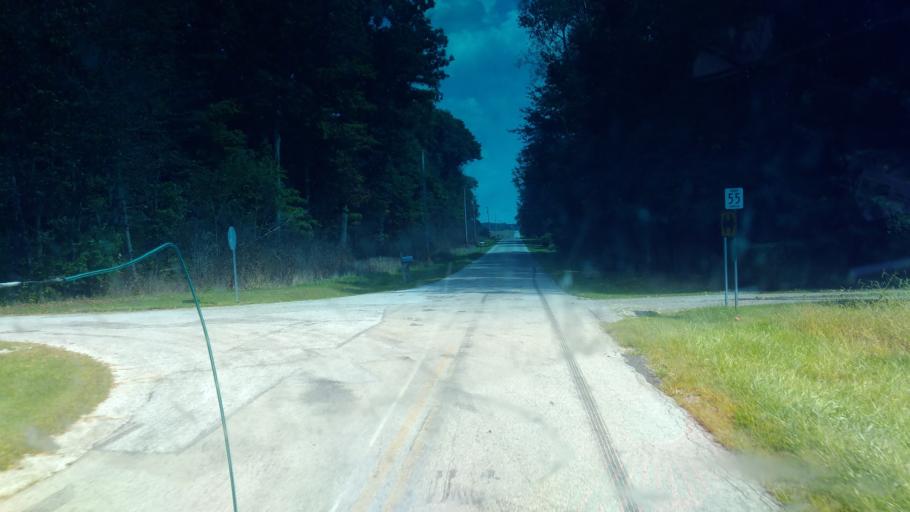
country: US
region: Ohio
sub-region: Hardin County
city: Ada
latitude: 40.7186
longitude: -83.8043
